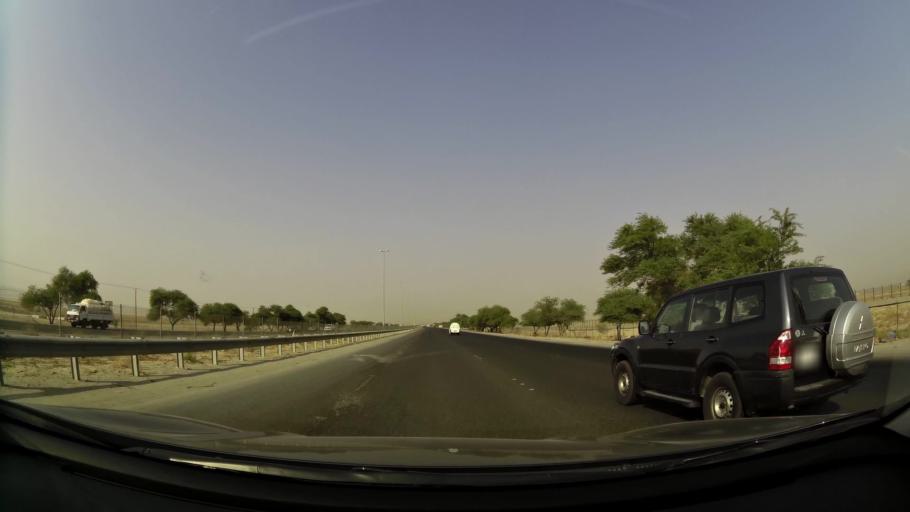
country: KW
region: Al Farwaniyah
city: Janub as Surrah
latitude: 29.1813
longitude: 47.9787
